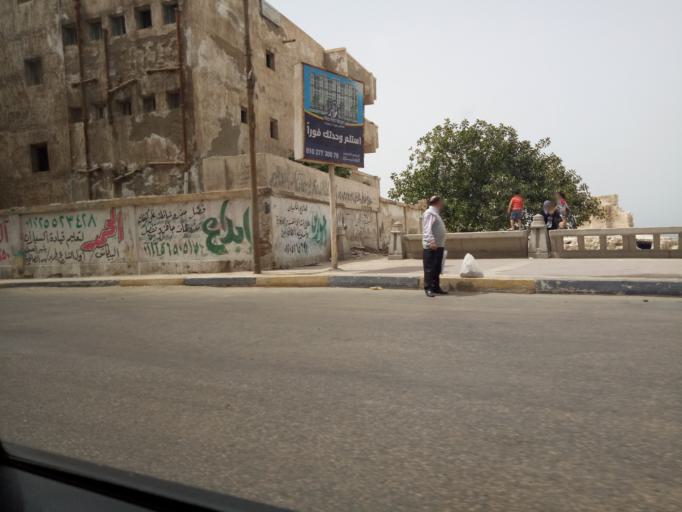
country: EG
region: Alexandria
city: Alexandria
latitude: 31.1359
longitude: 29.8190
